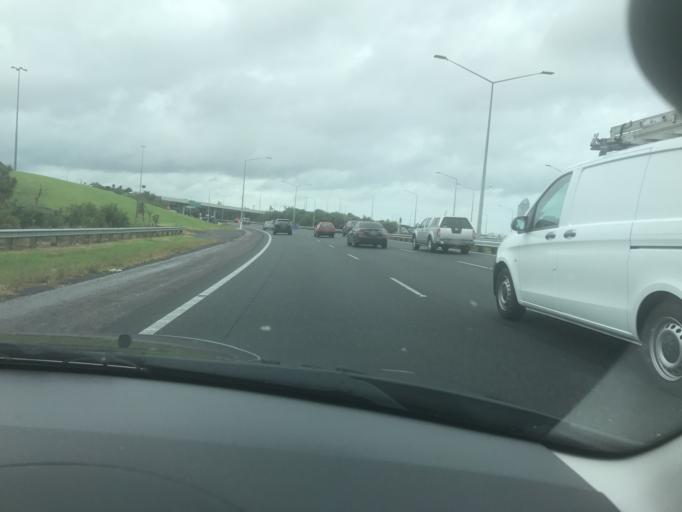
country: NZ
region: Auckland
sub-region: Auckland
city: North Shore
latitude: -36.8018
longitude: 174.7611
